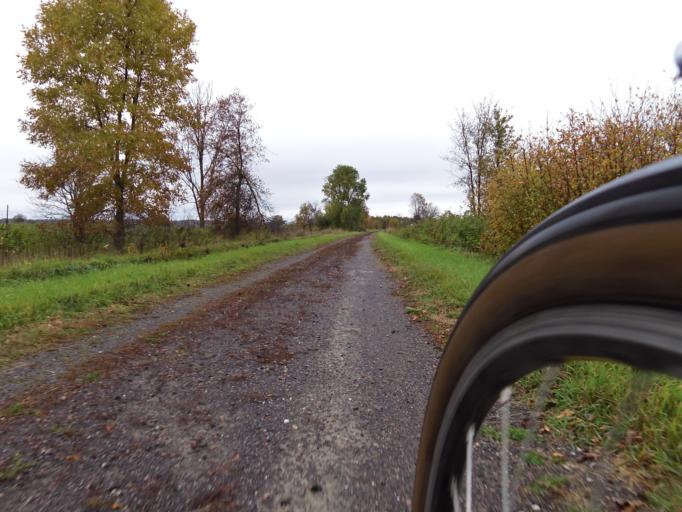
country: CA
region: Quebec
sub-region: Outaouais
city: Shawville
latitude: 45.7087
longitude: -76.5881
